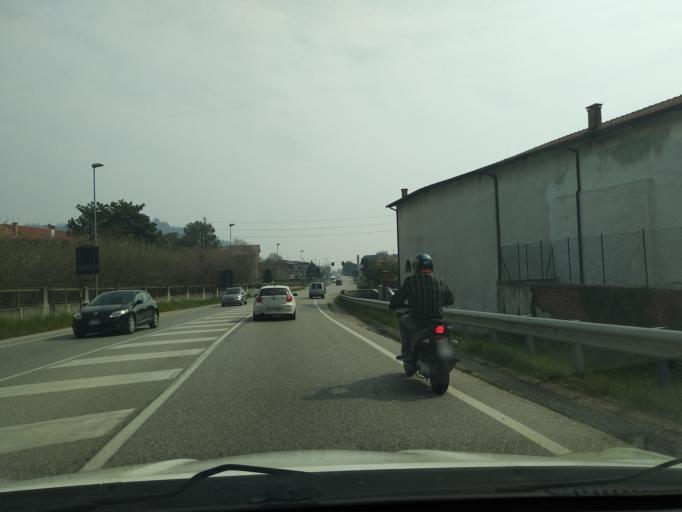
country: IT
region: Veneto
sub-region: Provincia di Vicenza
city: Chiampo
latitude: 45.5376
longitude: 11.2944
